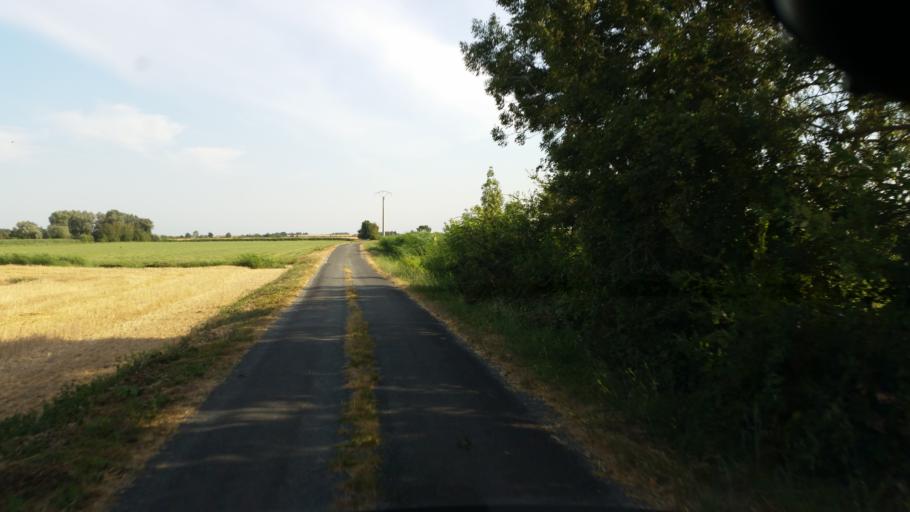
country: FR
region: Poitou-Charentes
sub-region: Departement de la Charente-Maritime
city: Marans
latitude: 46.3141
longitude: -0.9465
